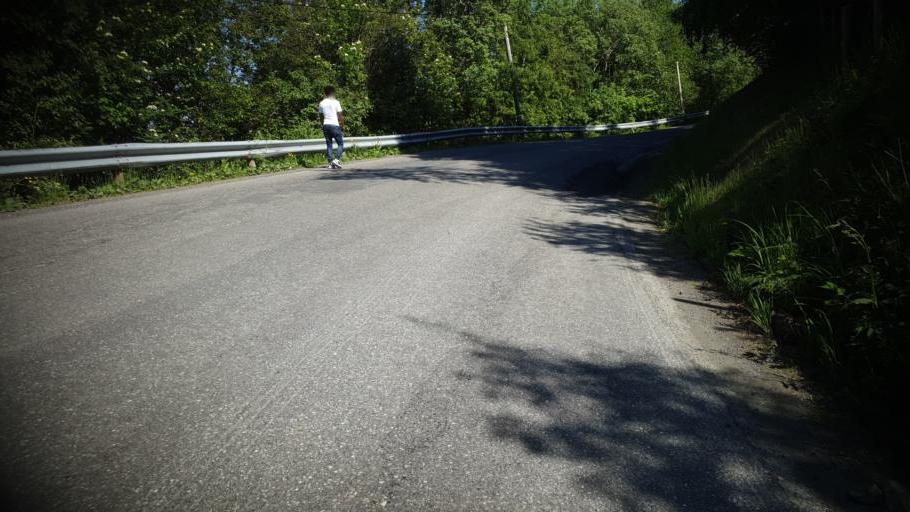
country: NO
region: Sor-Trondelag
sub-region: Malvik
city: Malvik
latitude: 63.4321
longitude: 10.5980
